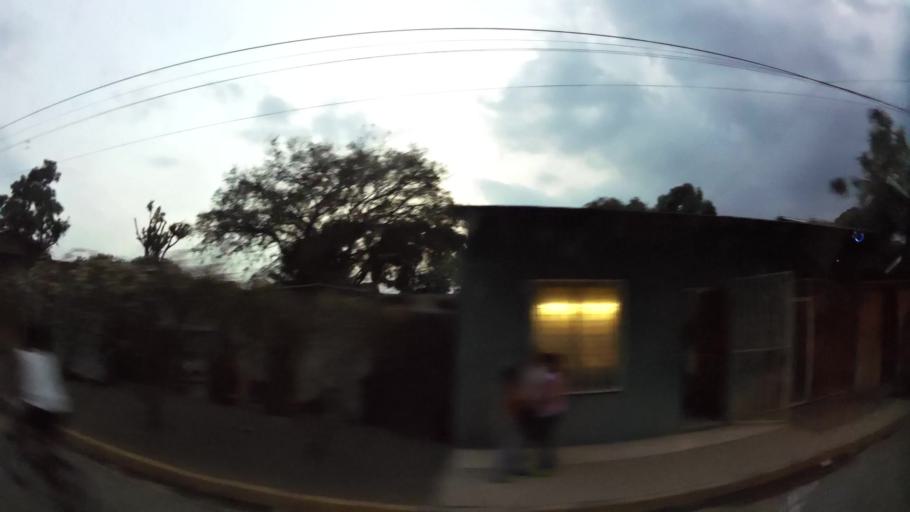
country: NI
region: Matagalpa
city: Ciudad Dario
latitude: 12.8534
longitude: -86.0961
